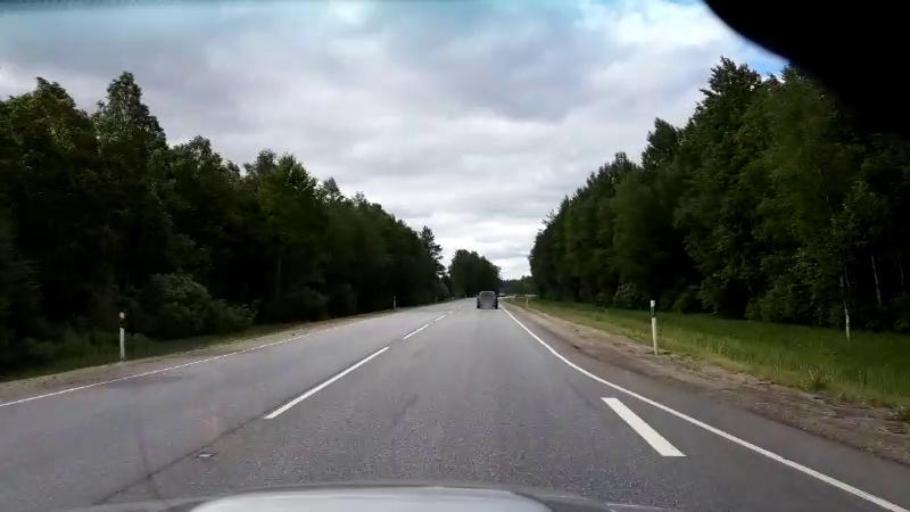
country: EE
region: Raplamaa
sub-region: Maerjamaa vald
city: Marjamaa
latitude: 58.9455
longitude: 24.4676
